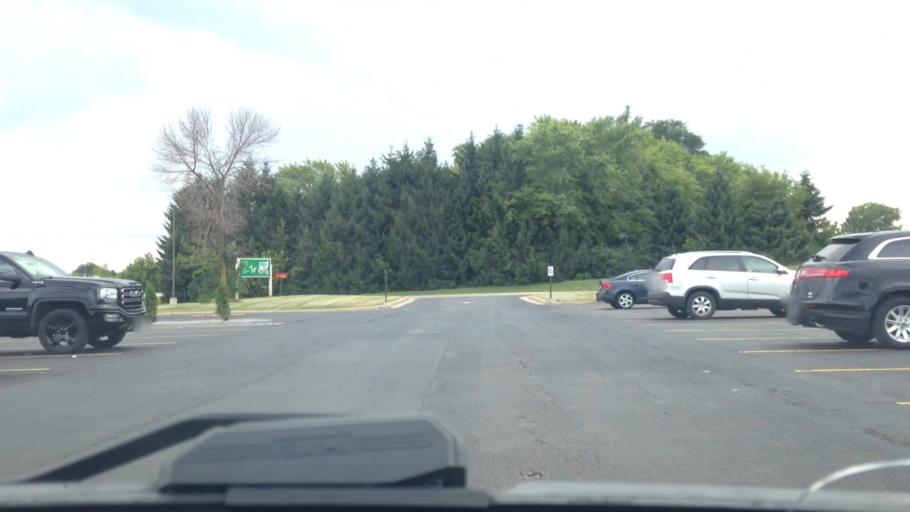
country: US
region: Wisconsin
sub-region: Washington County
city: Richfield
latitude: 43.2818
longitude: -88.1977
